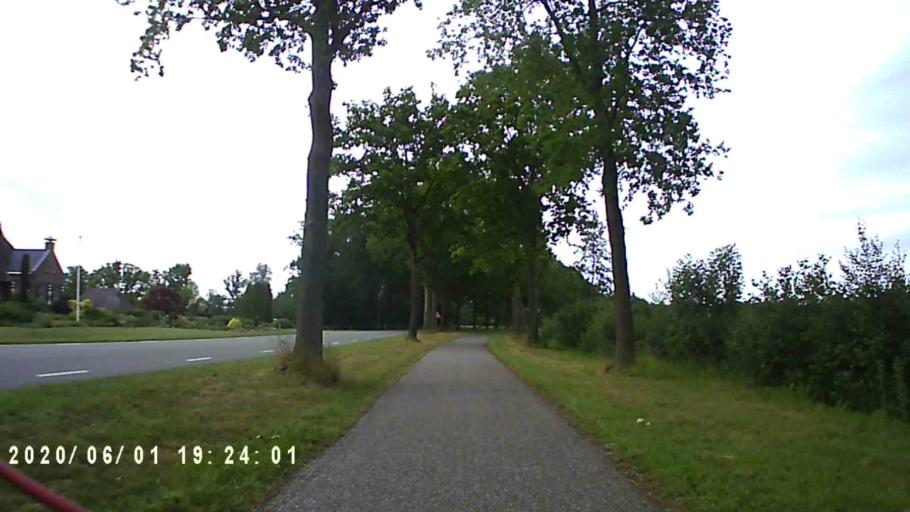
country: NL
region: Friesland
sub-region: Gemeente Achtkarspelen
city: Drogeham
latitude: 53.2047
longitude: 6.1274
